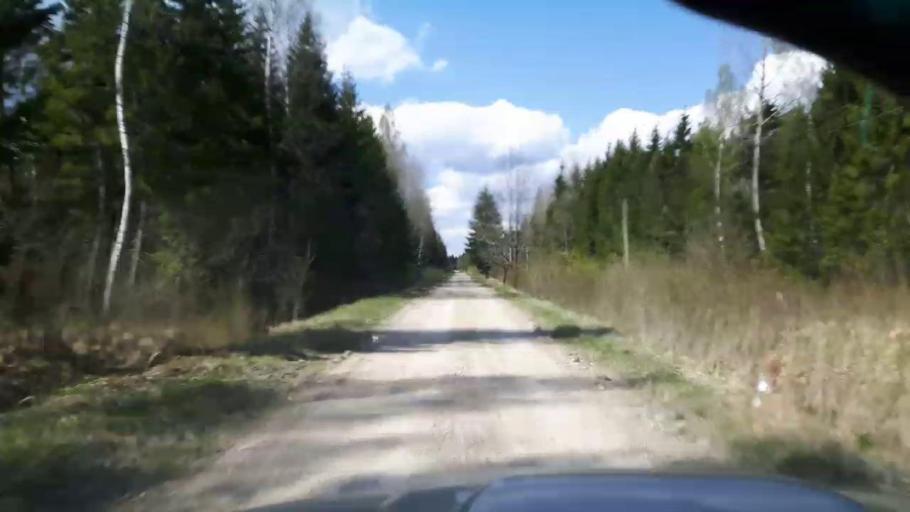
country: EE
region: Paernumaa
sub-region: Tootsi vald
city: Tootsi
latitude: 58.4439
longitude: 24.9179
